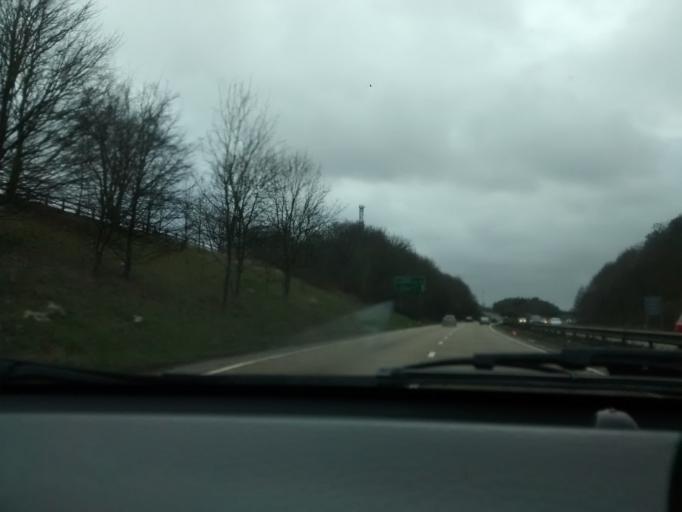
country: GB
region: England
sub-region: Suffolk
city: Ipswich
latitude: 52.0249
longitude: 1.1478
